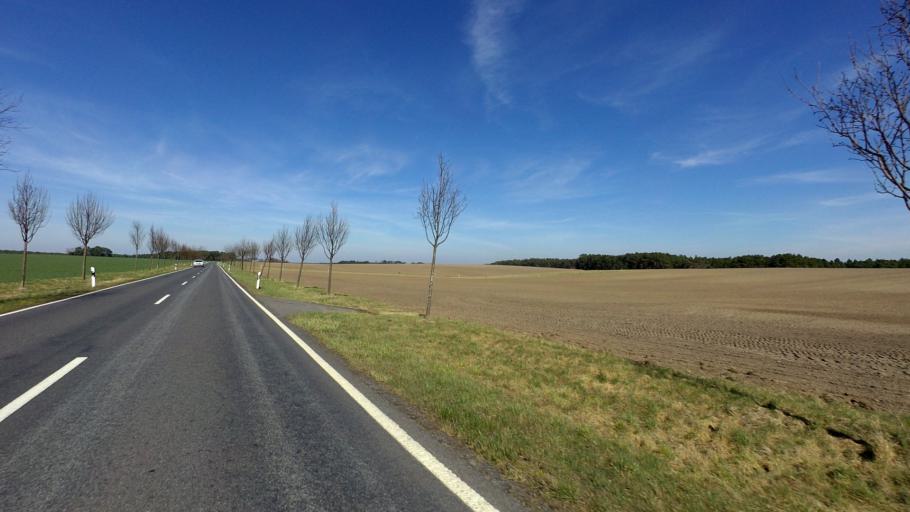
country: DE
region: Brandenburg
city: Munchehofe
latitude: 52.1762
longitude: 13.9192
